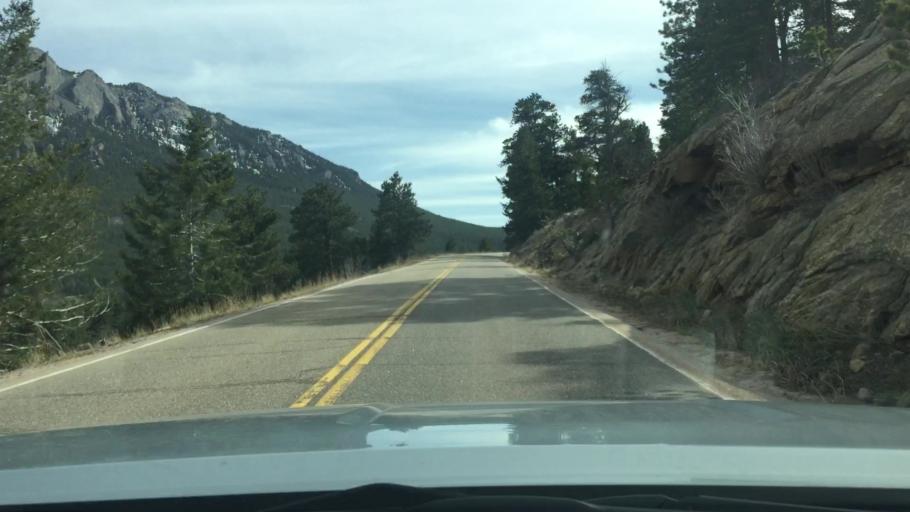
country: US
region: Colorado
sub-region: Larimer County
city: Estes Park
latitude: 40.3244
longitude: -105.5310
